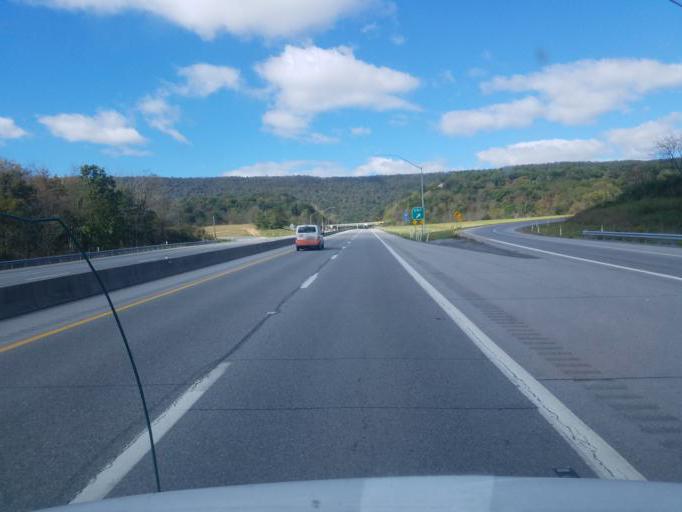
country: US
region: Pennsylvania
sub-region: Bedford County
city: Everett
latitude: 40.0245
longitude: -78.3621
